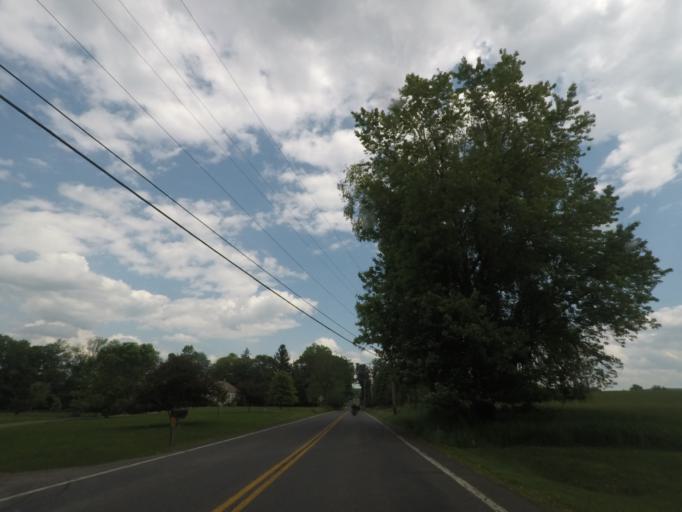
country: US
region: New York
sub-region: Dutchess County
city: Pine Plains
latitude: 42.0517
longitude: -73.6272
